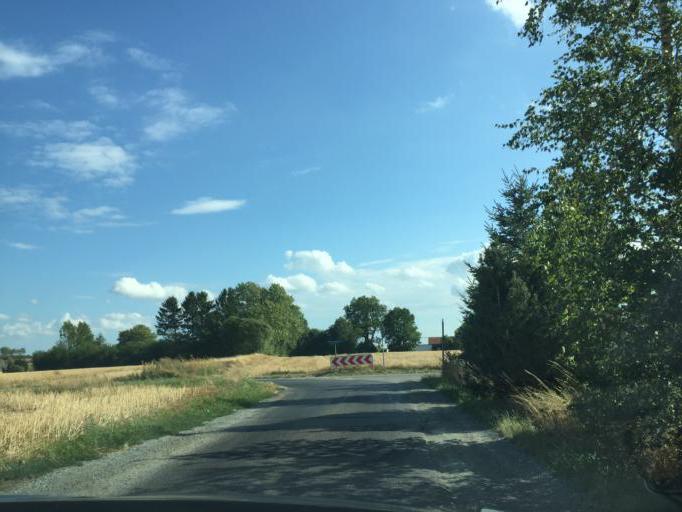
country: DK
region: South Denmark
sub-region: Faaborg-Midtfyn Kommune
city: Arslev
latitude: 55.3082
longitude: 10.4305
